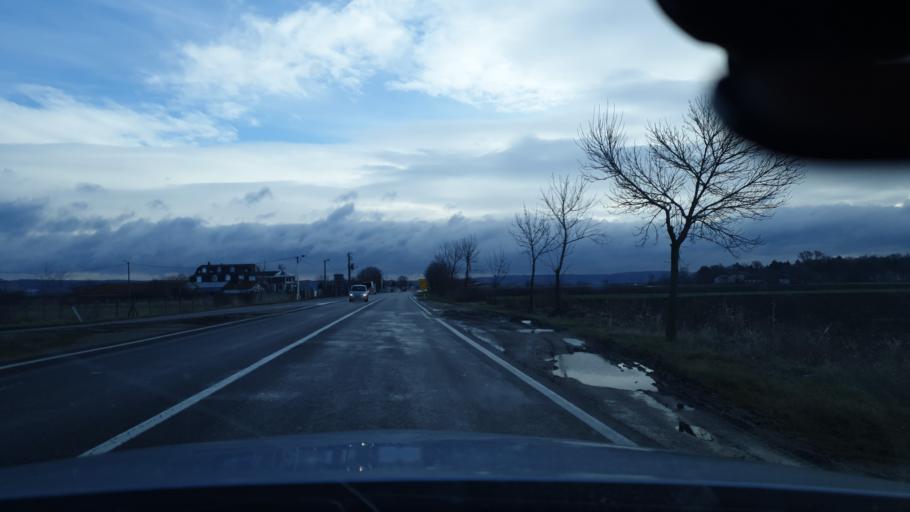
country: RS
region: Central Serbia
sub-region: Branicevski Okrug
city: Pozarevac
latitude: 44.6022
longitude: 21.1386
